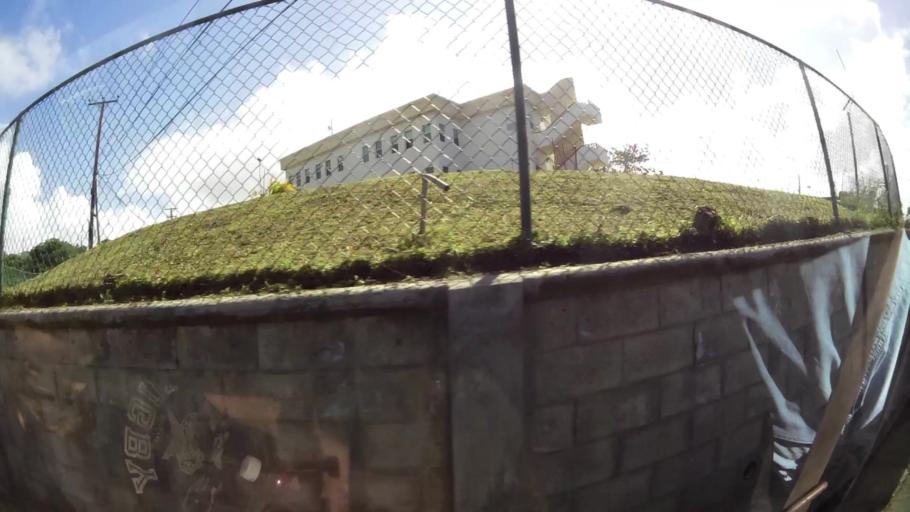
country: MS
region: Saint Peter
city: Brades
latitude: 16.7902
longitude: -62.2119
